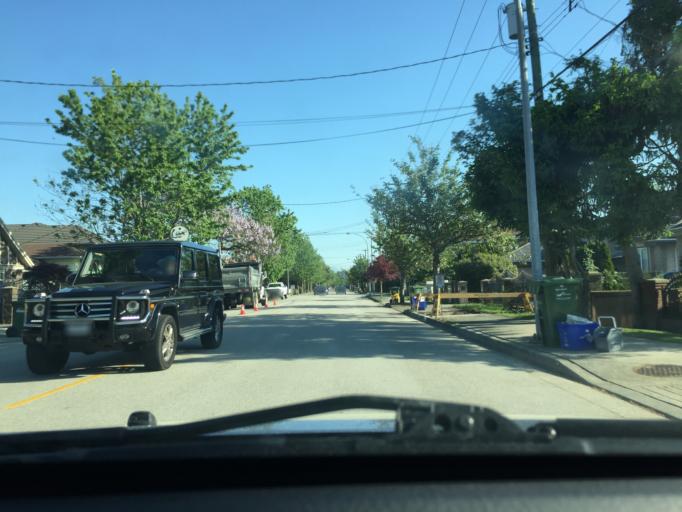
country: CA
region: British Columbia
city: Richmond
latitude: 49.1504
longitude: -123.1309
